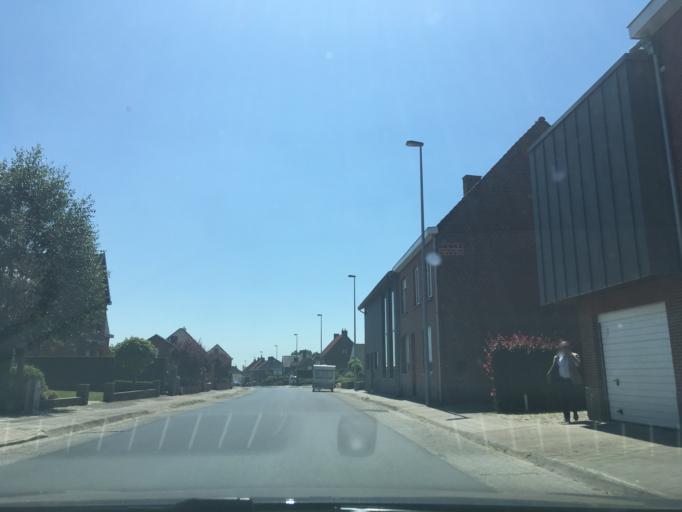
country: BE
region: Flanders
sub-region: Provincie West-Vlaanderen
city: Ardooie
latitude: 51.0052
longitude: 3.2086
